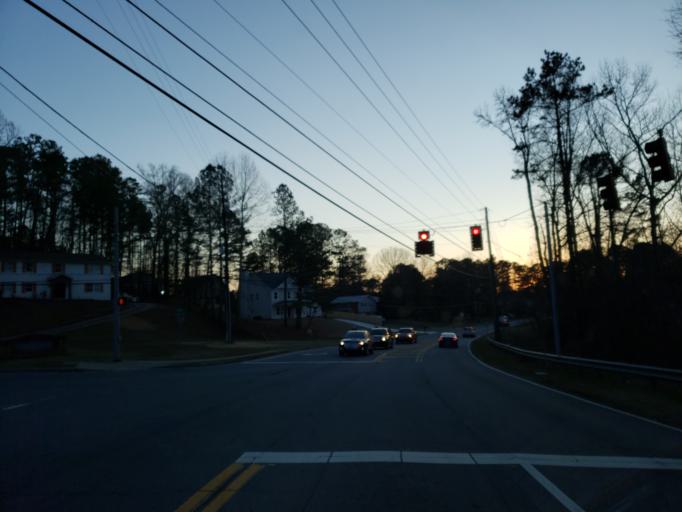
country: US
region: Georgia
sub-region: Cherokee County
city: Woodstock
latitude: 34.1065
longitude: -84.4969
